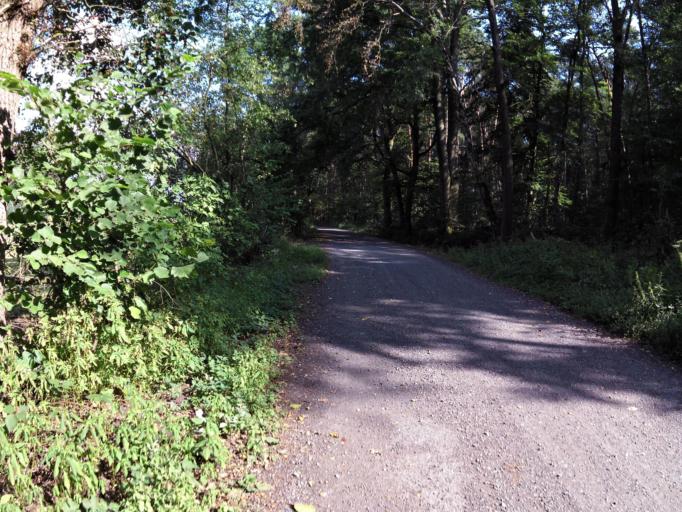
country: DE
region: North Rhine-Westphalia
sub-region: Regierungsbezirk Munster
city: Warendorf
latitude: 51.9372
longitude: 7.9259
